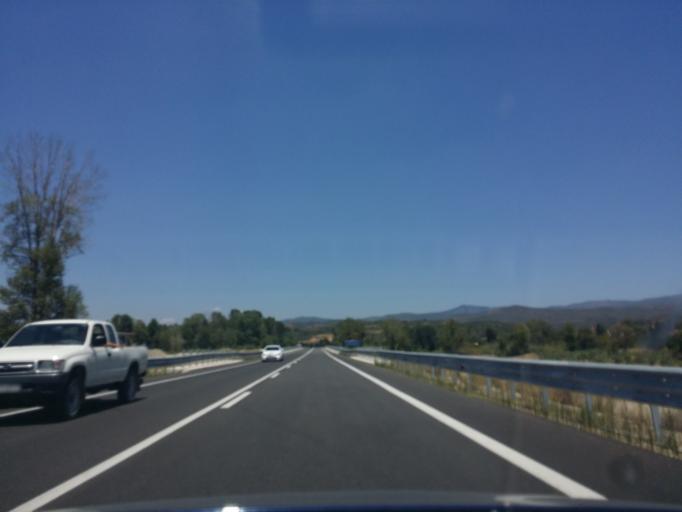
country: GR
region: Peloponnese
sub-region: Nomos Lakonias
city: Sparti
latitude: 37.0097
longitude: 22.4845
